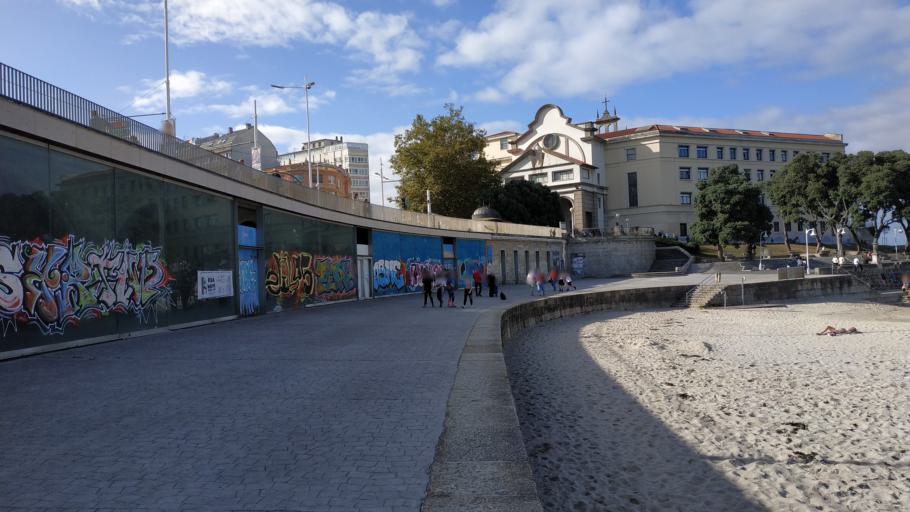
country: ES
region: Galicia
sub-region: Provincia da Coruna
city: A Coruna
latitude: 43.3693
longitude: -8.4145
